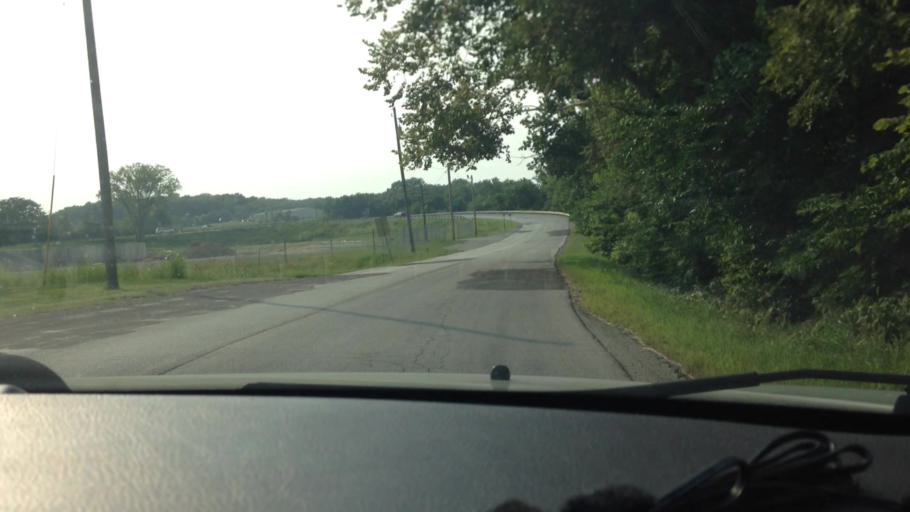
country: US
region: Missouri
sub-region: Platte County
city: Platte City
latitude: 39.3847
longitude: -94.7853
